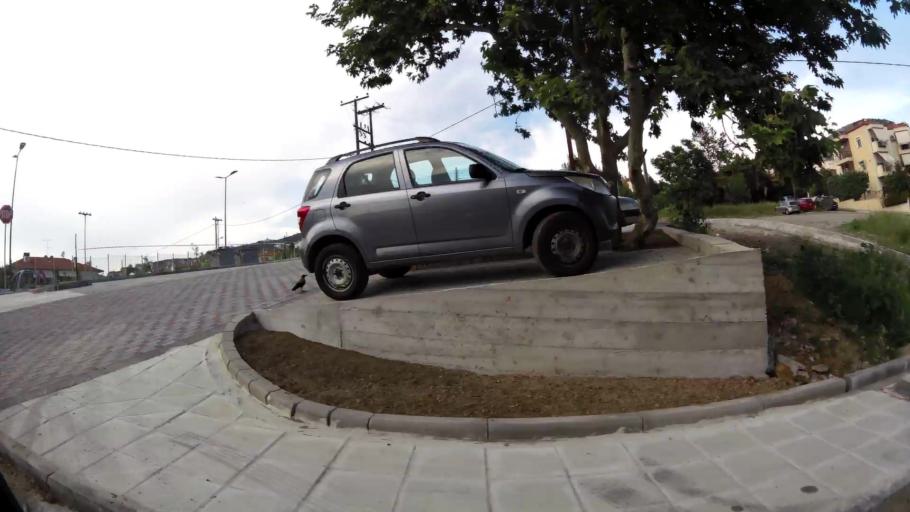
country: GR
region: Central Macedonia
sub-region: Nomos Thessalonikis
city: Pefka
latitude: 40.6544
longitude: 22.9997
